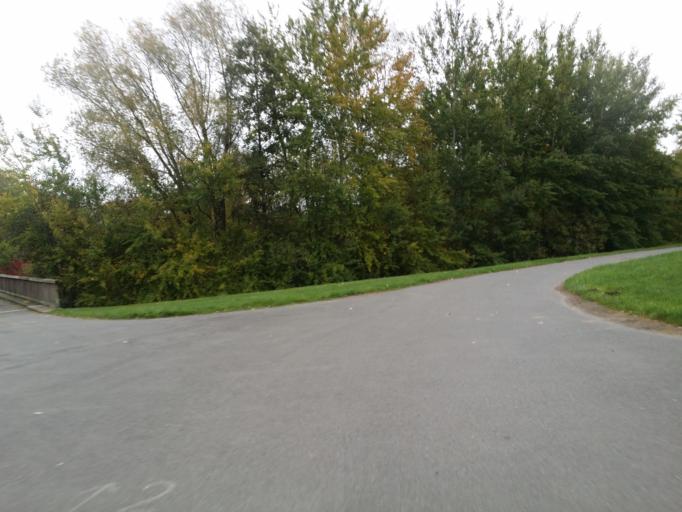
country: DE
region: Lower Saxony
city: Stuhr
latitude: 53.0582
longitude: 8.7539
